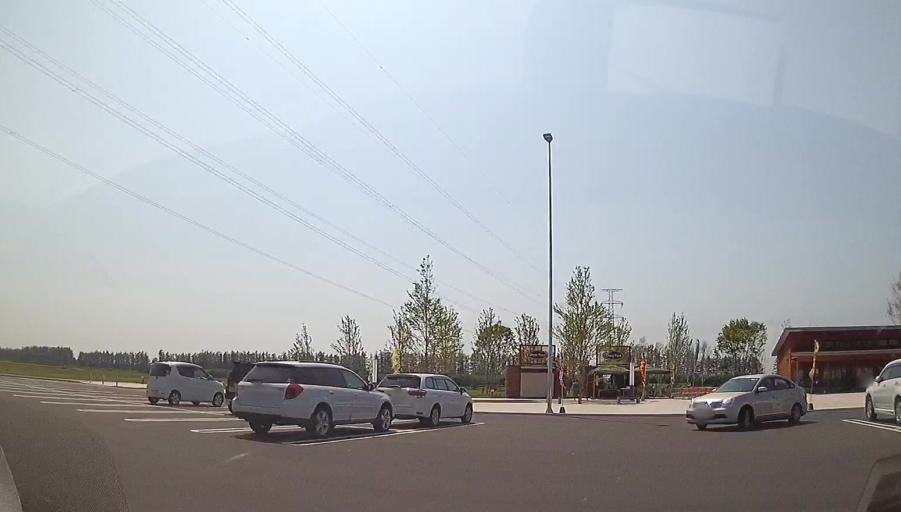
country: JP
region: Hokkaido
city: Otofuke
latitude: 43.1440
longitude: 143.2399
